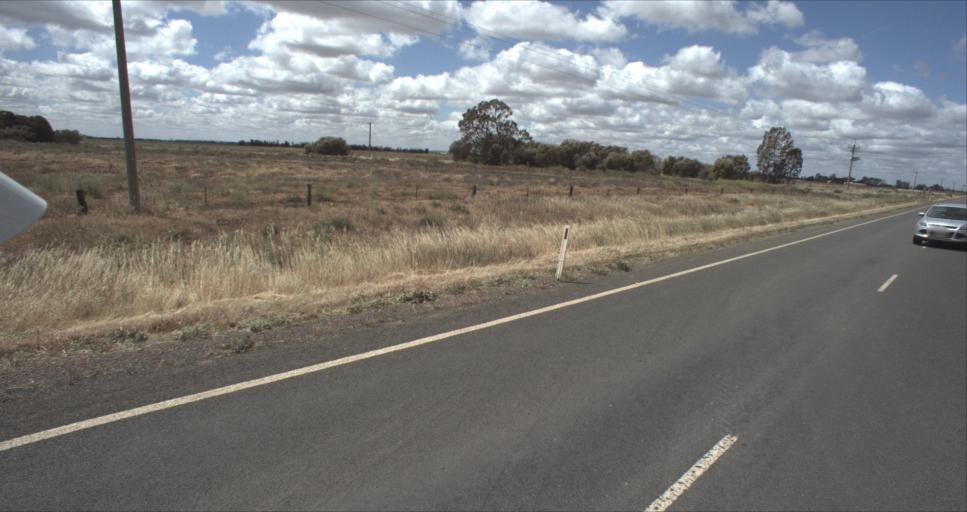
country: AU
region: New South Wales
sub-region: Murrumbidgee Shire
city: Darlington Point
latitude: -34.4862
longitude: 146.1598
